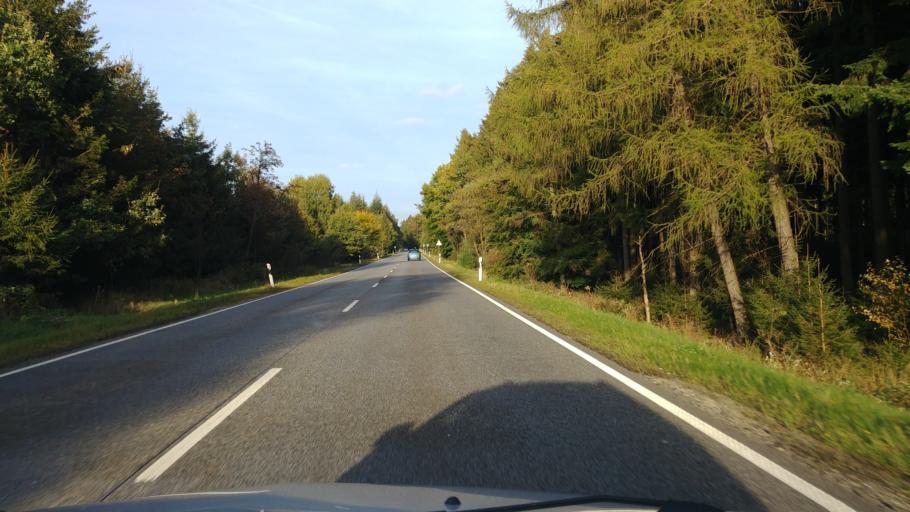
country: DE
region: Rheinland-Pfalz
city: Kleinich
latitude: 49.8620
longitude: 7.1819
